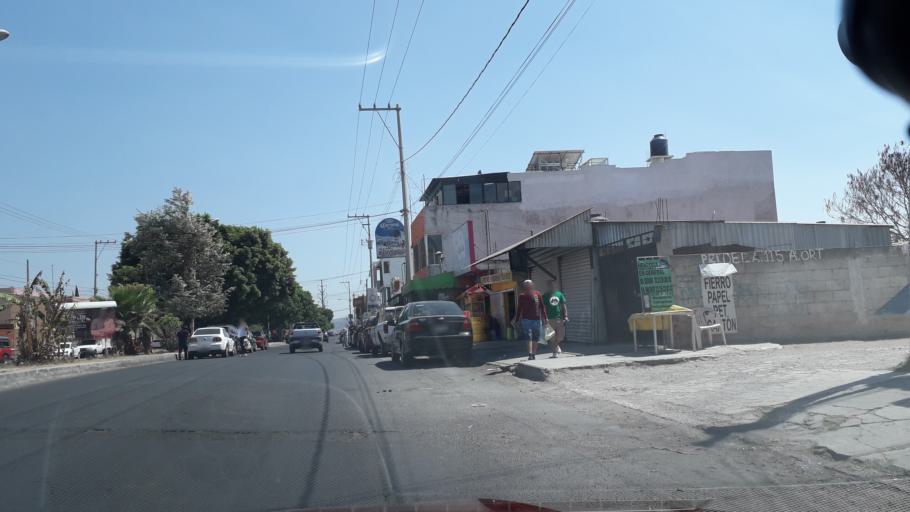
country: MX
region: Puebla
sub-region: Puebla
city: El Capulo (La Quebradora)
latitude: 18.9732
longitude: -98.2187
